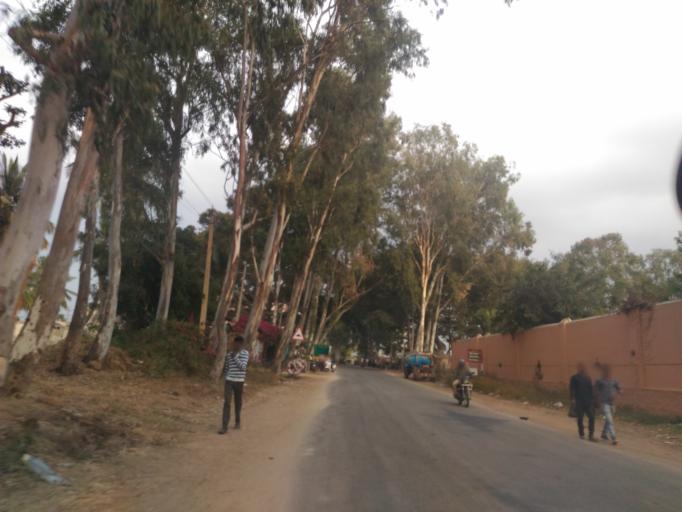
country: IN
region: Karnataka
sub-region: Chikkaballapur
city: Chik Ballapur
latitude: 13.3483
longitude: 77.6855
